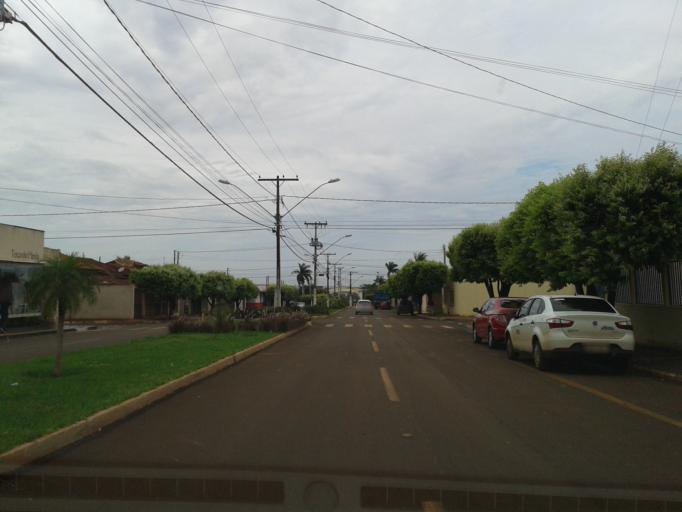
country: BR
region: Goias
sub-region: Itumbiara
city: Itumbiara
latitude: -18.4296
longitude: -49.1882
